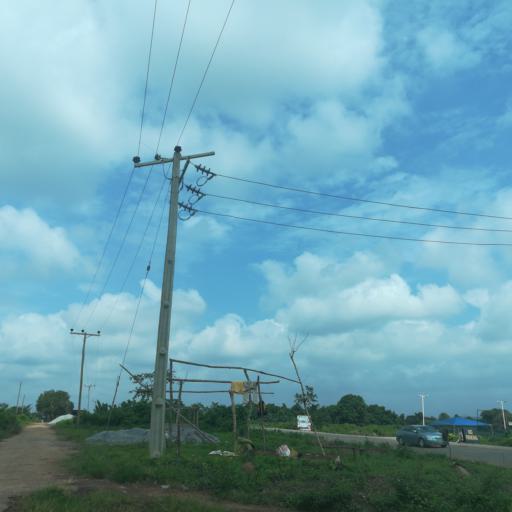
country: NG
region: Lagos
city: Ikorodu
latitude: 6.6523
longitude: 3.7010
